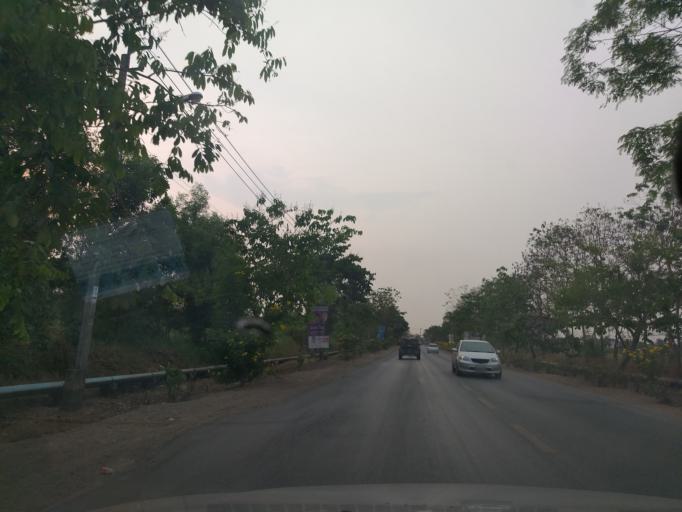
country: TH
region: Bangkok
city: Nong Chok
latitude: 13.8371
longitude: 100.9050
